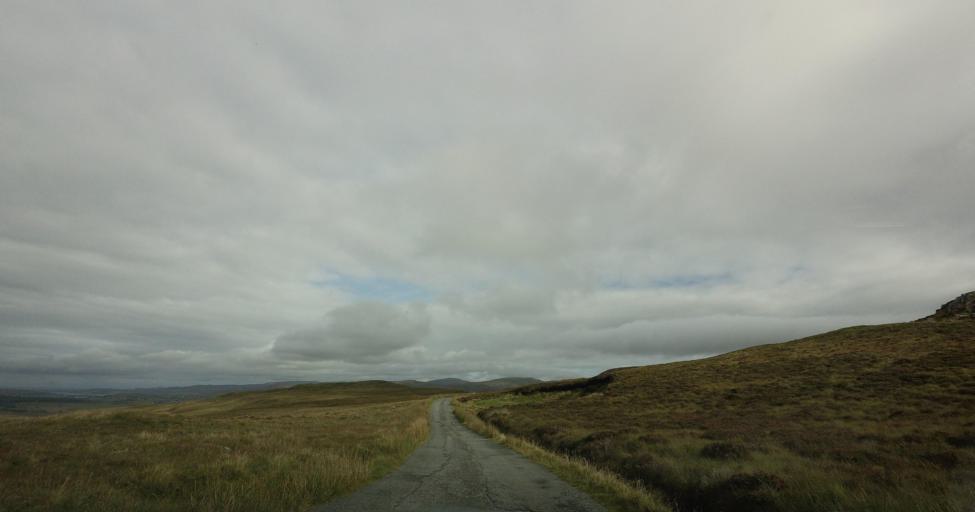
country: GB
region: Scotland
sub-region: Highland
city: Isle of Skye
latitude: 57.4055
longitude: -6.2665
